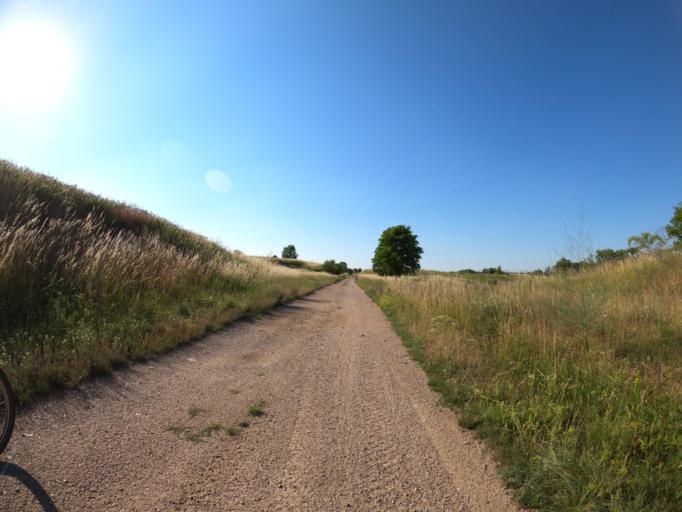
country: DE
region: Brandenburg
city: Gartz
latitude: 53.2177
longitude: 14.3754
